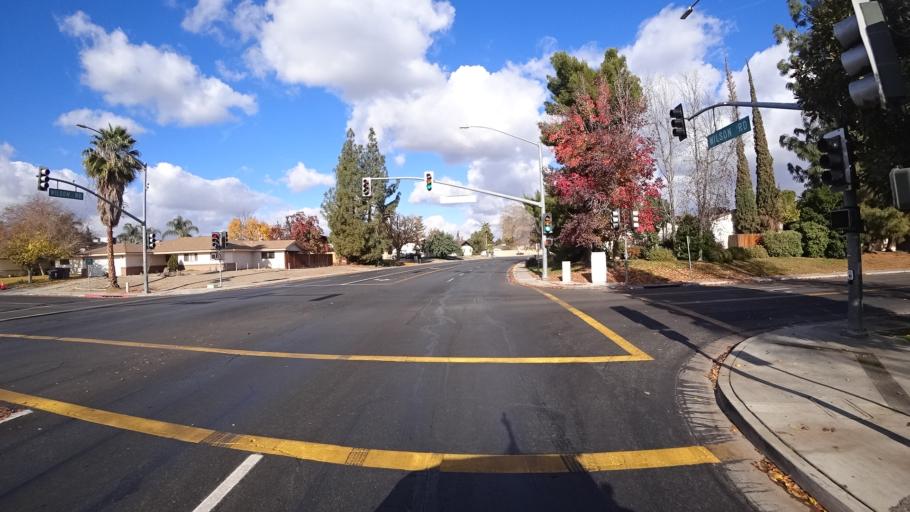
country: US
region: California
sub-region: Kern County
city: Bakersfield
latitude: 35.3298
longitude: -119.0655
